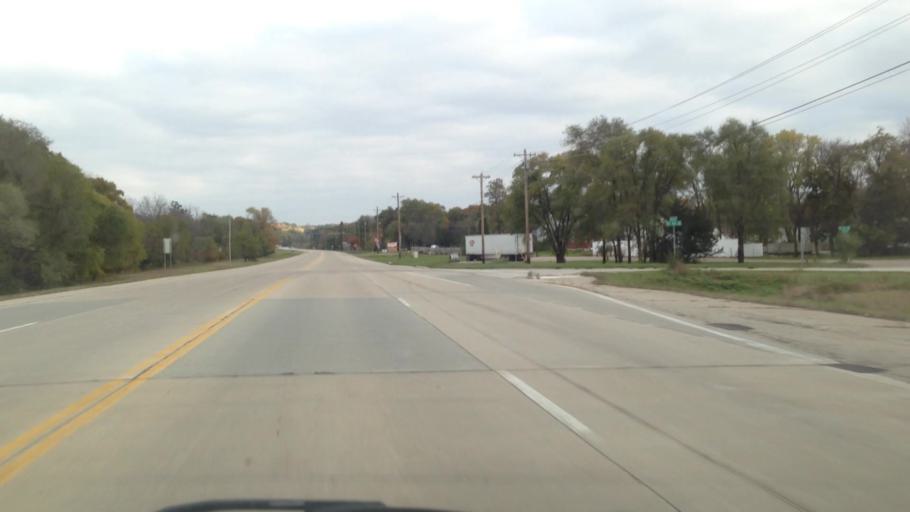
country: US
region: Minnesota
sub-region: Olmsted County
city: Rochester
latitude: 43.9907
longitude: -92.4179
